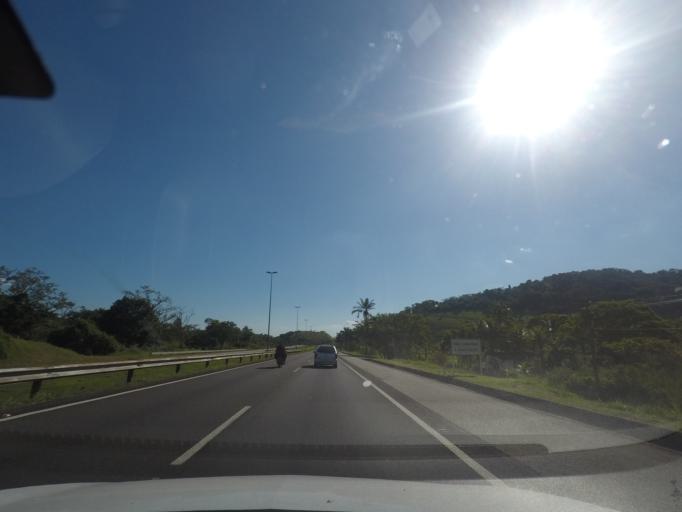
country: BR
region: Rio de Janeiro
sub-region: Guapimirim
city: Guapimirim
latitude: -22.6314
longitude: -43.0522
